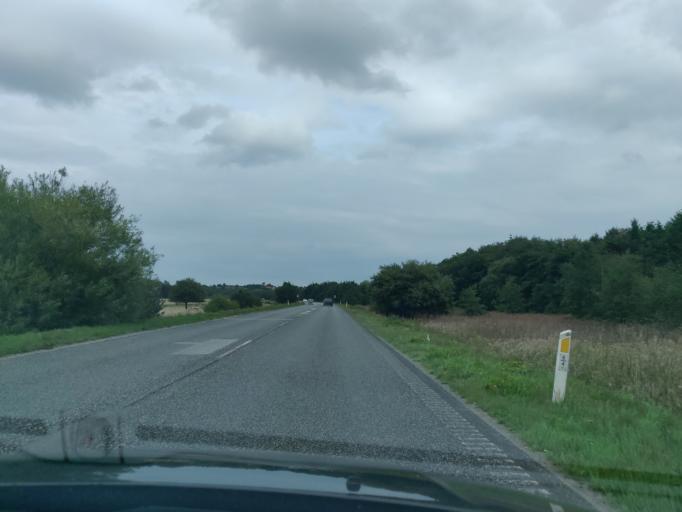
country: DK
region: North Denmark
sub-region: Alborg Kommune
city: Svenstrup
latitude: 57.0132
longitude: 9.8610
